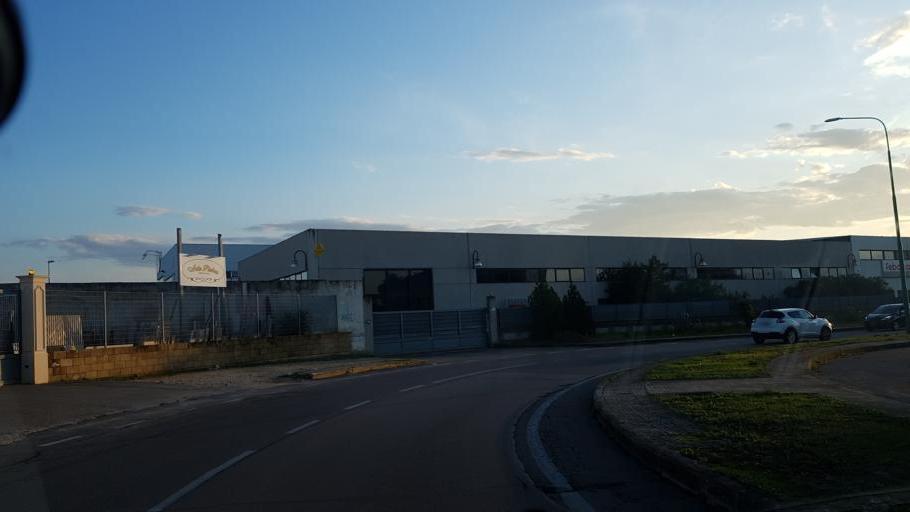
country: IT
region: Apulia
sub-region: Provincia di Lecce
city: Giorgilorio
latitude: 40.3818
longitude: 18.1401
